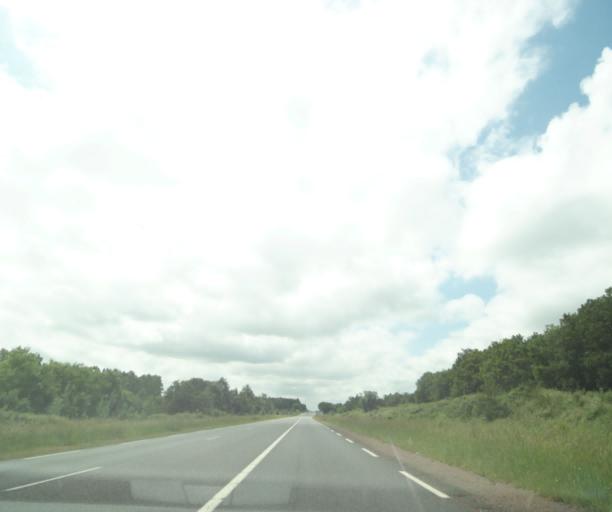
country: FR
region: Poitou-Charentes
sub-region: Departement des Deux-Sevres
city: Airvault
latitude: 46.8018
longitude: -0.2124
